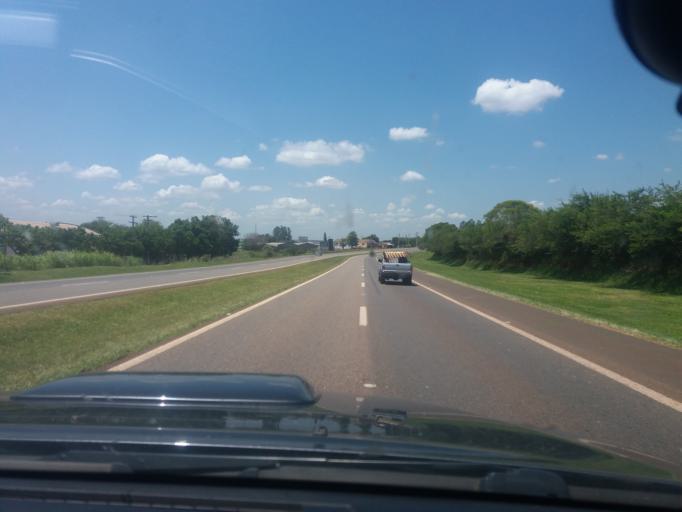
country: BR
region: Sao Paulo
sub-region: Tatui
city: Tatui
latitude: -23.3545
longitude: -47.8804
